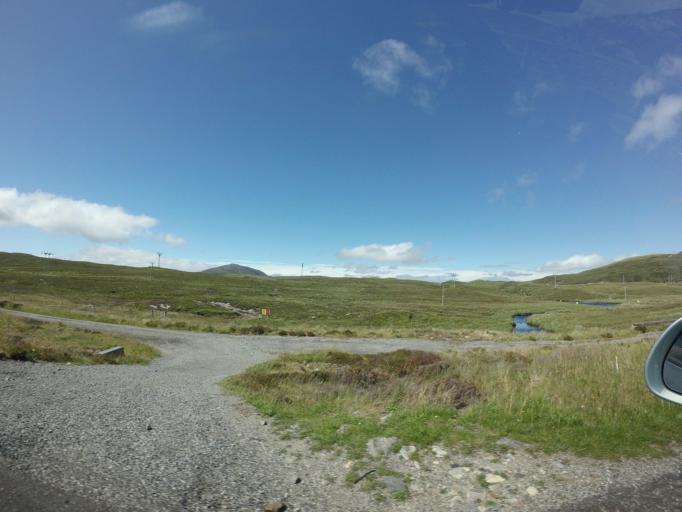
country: GB
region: Scotland
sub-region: Eilean Siar
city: Harris
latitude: 58.0831
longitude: -6.6439
